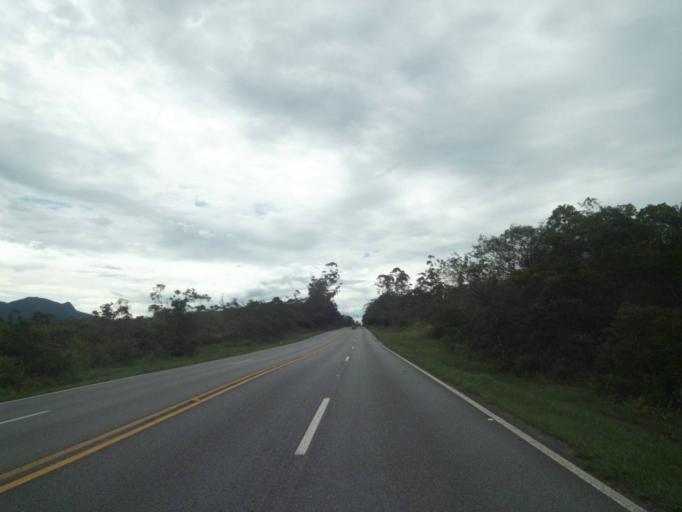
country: BR
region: Parana
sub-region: Pontal Do Parana
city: Pontal do Parana
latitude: -25.6104
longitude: -48.6050
